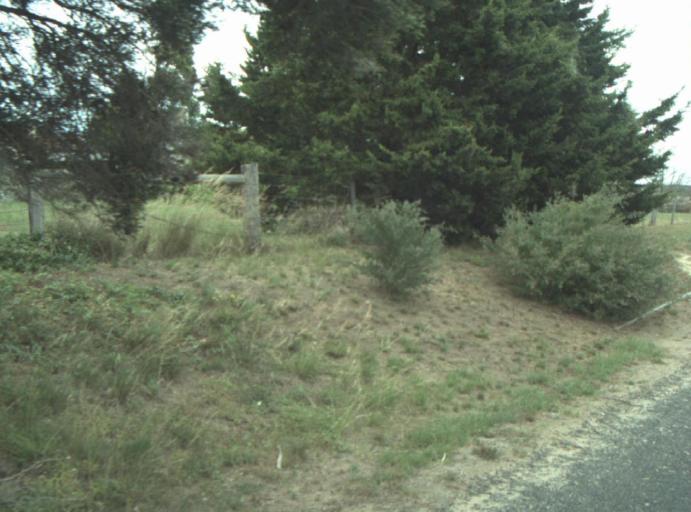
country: AU
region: Victoria
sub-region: Queenscliffe
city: Queenscliff
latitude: -38.2684
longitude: 144.6066
